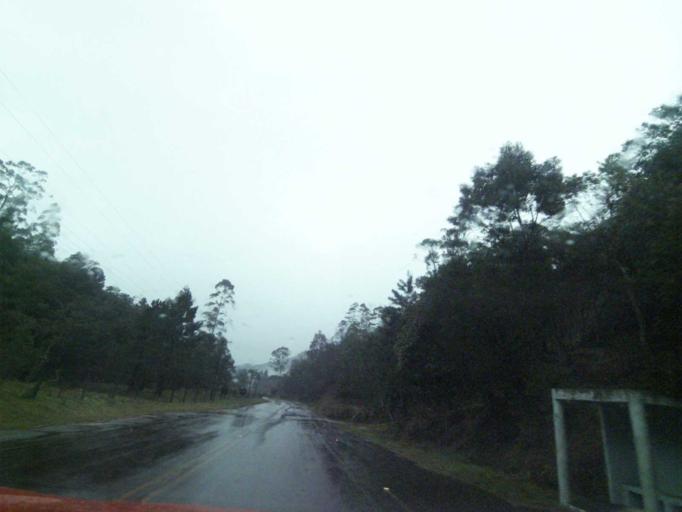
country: BR
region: Santa Catarina
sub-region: Anitapolis
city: Anitapolis
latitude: -27.8237
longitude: -49.0497
